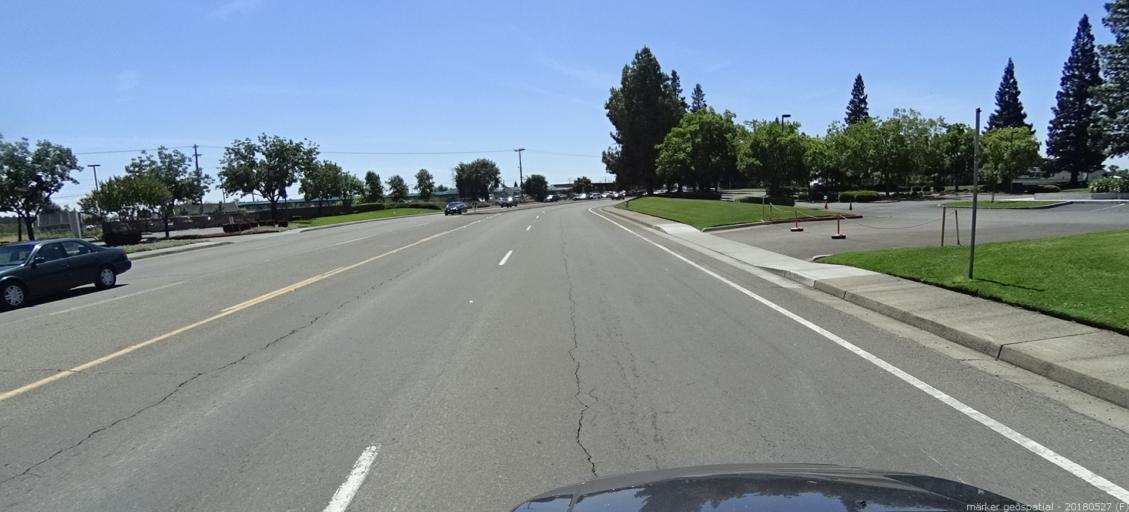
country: US
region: California
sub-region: Sacramento County
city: Rosemont
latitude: 38.5461
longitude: -121.3920
